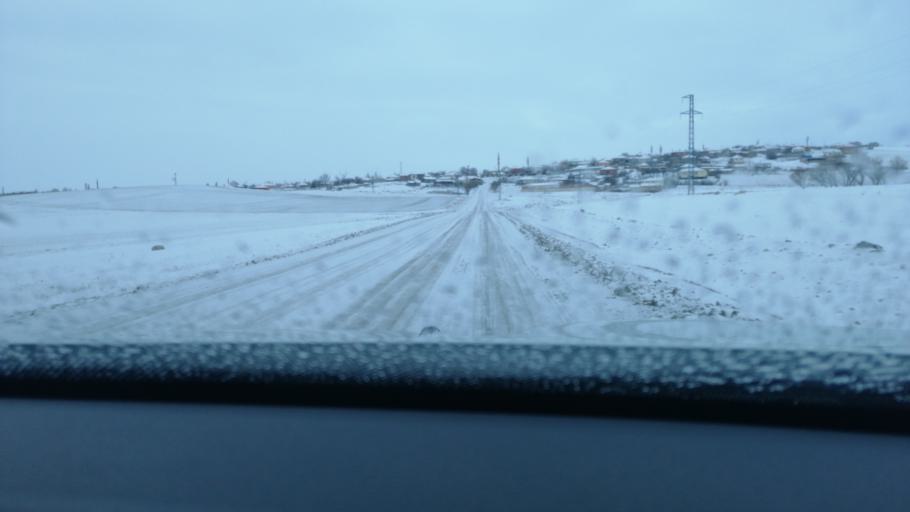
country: TR
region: Aksaray
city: Agacoren
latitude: 38.9408
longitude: 33.9476
